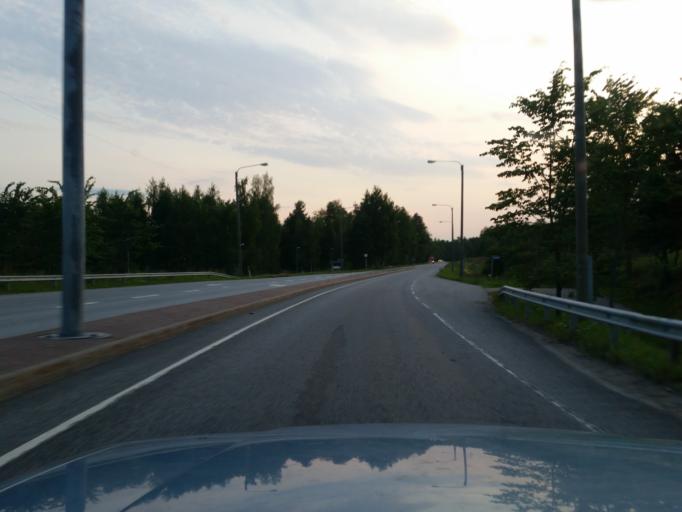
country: FI
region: Southern Savonia
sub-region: Savonlinna
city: Savonlinna
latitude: 61.8777
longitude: 28.8188
